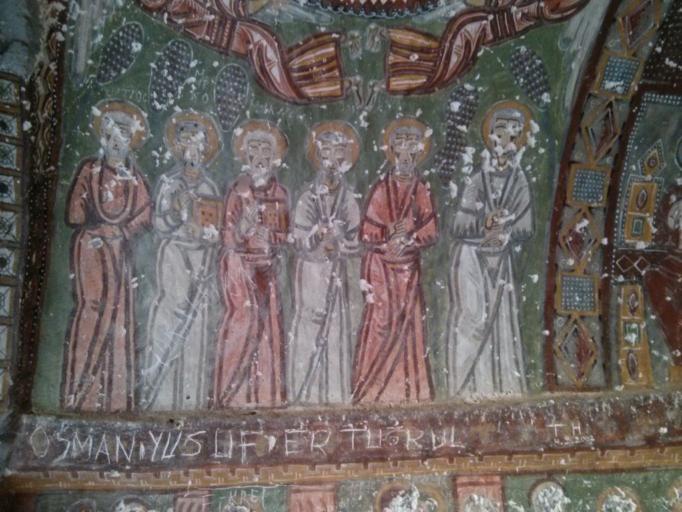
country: TR
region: Aksaray
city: Guzelyurt
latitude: 38.2498
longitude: 34.3109
